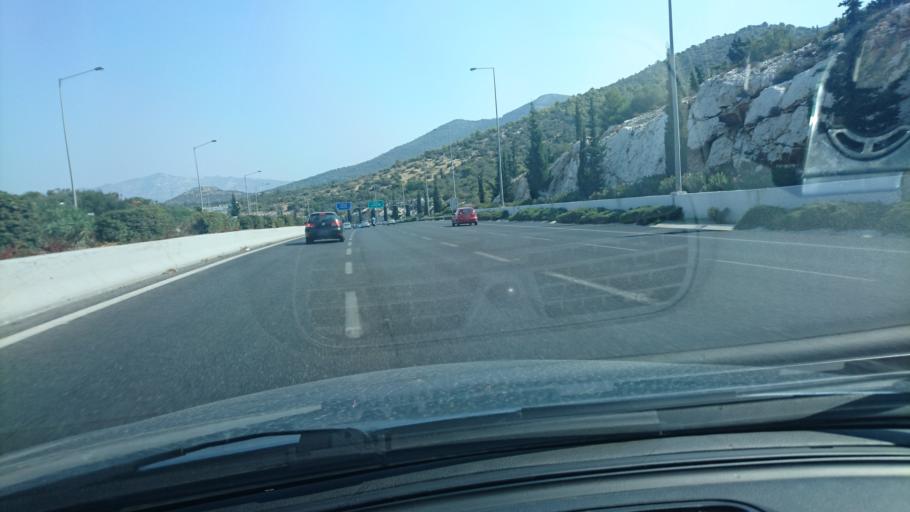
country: GR
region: Attica
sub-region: Nomos Attikis
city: Zografos
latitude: 37.9704
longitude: 23.7917
